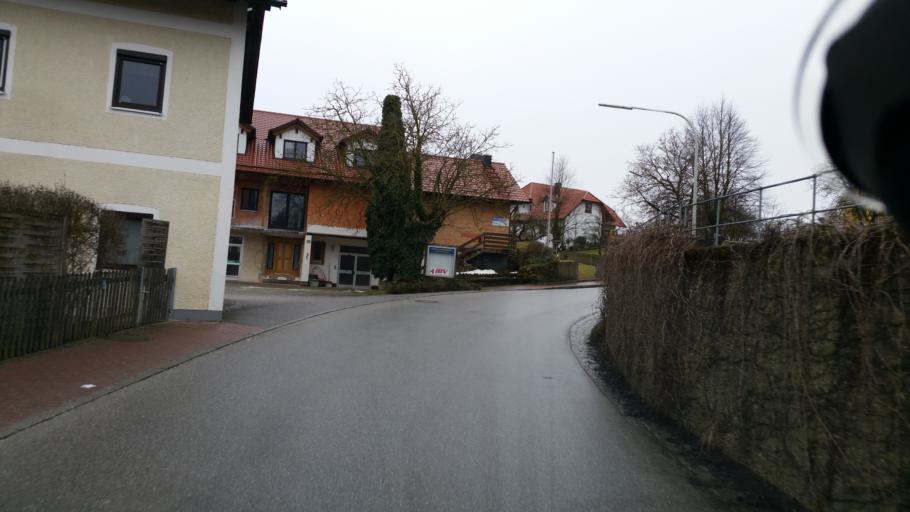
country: DE
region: Bavaria
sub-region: Lower Bavaria
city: Tiefenbach
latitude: 48.4839
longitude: 12.0919
